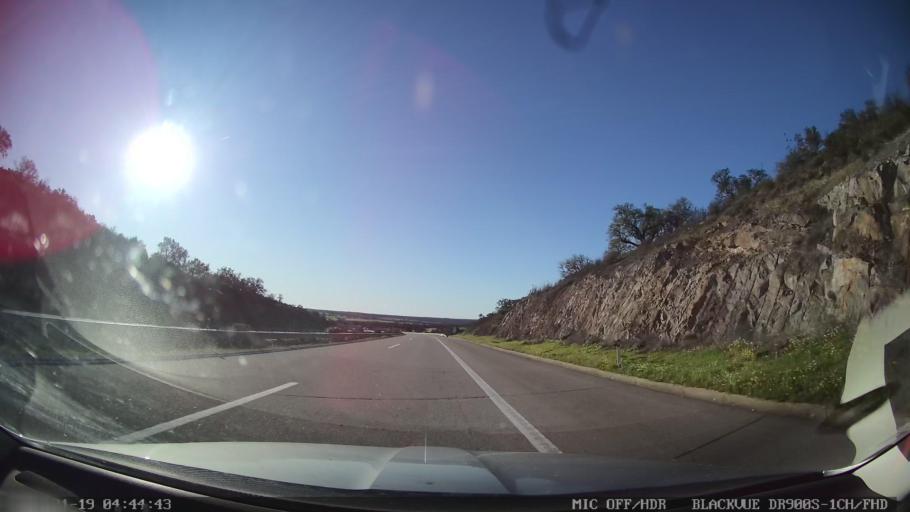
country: PT
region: Evora
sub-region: Montemor-O-Novo
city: Montemor-o-Novo
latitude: 38.6703
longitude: -8.2211
